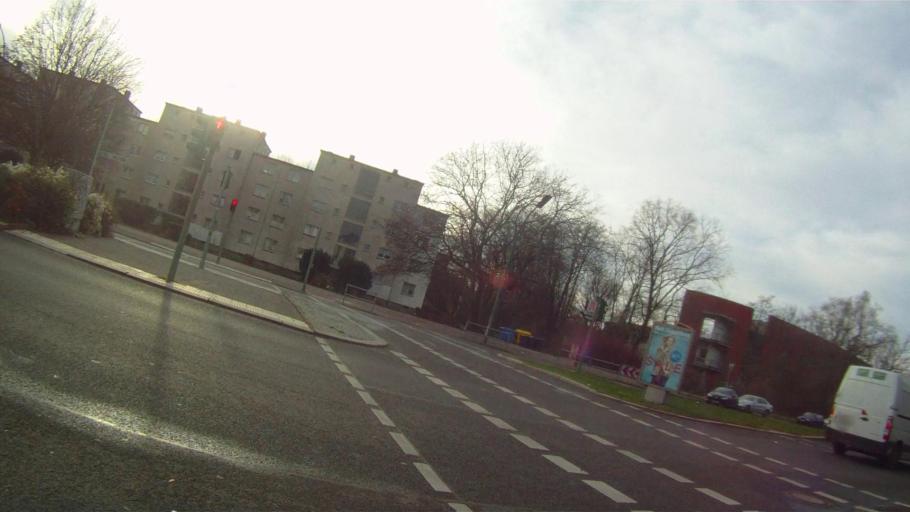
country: DE
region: Berlin
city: Britz
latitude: 52.4460
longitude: 13.4447
